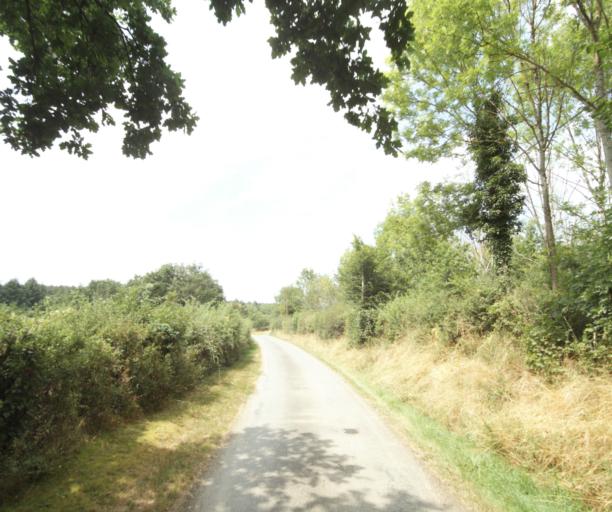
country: FR
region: Bourgogne
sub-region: Departement de Saone-et-Loire
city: Gueugnon
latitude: 46.5803
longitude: 4.0363
